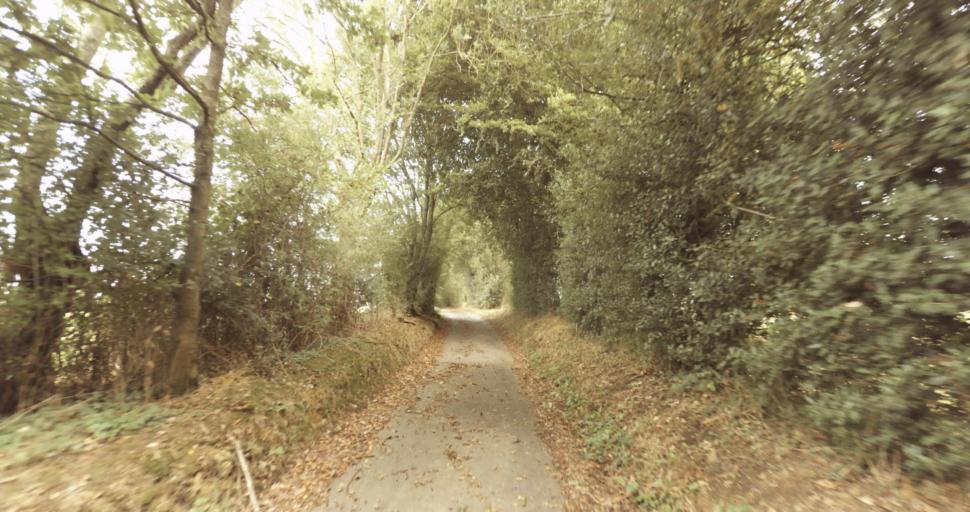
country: FR
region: Lower Normandy
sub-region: Departement de l'Orne
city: Sainte-Gauburge-Sainte-Colombe
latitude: 48.7257
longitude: 0.4423
